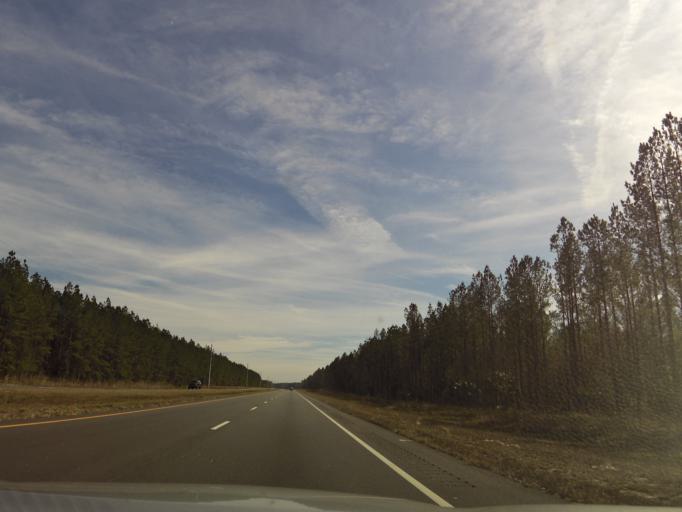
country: US
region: Georgia
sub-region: Glynn County
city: Dock Junction
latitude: 31.2294
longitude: -81.7415
